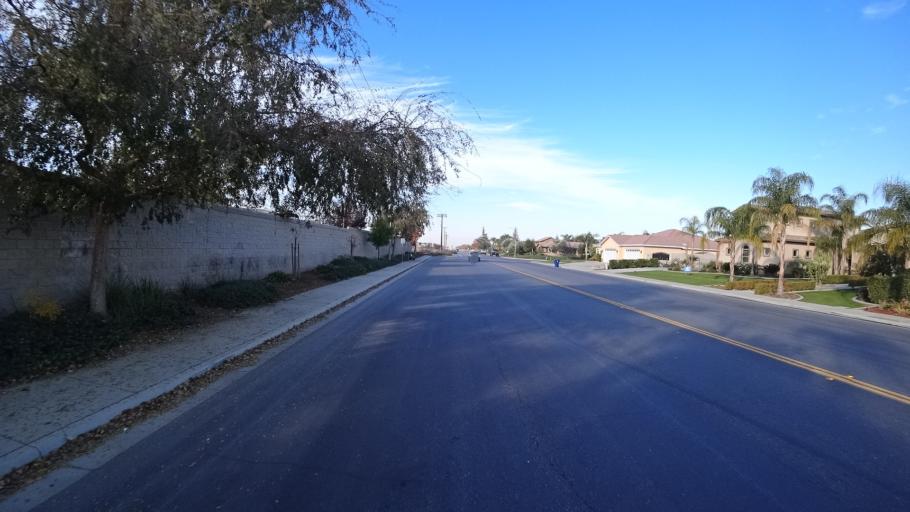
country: US
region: California
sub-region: Kern County
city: Rosedale
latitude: 35.4124
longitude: -119.1425
